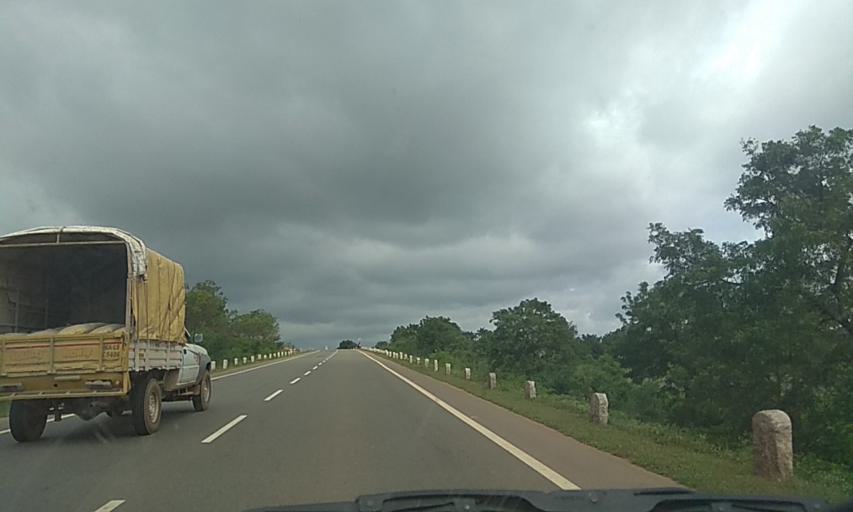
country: IN
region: Karnataka
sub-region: Dharwad
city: Hubli
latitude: 15.3411
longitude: 75.0823
